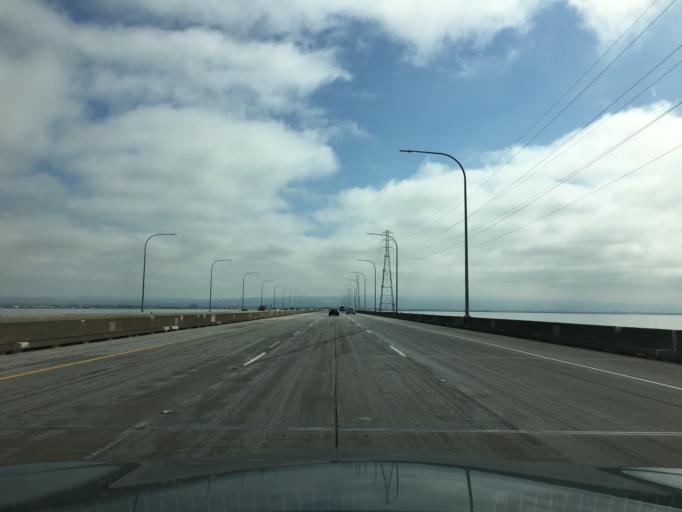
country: US
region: California
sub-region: Alameda County
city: San Lorenzo
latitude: 37.6095
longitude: -122.1798
